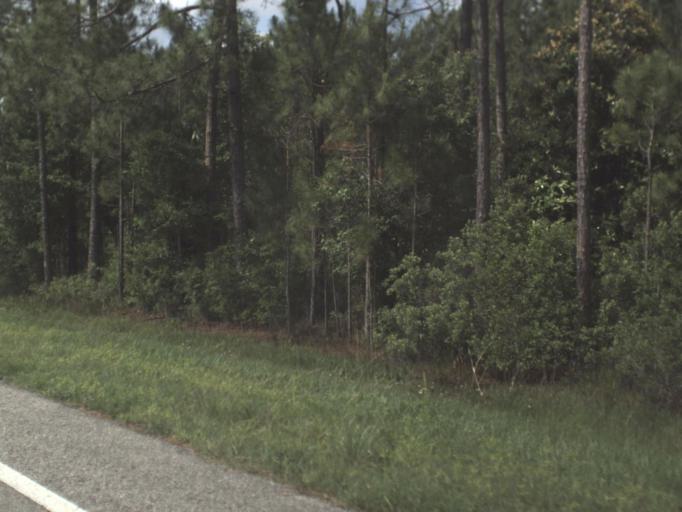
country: US
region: Florida
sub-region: Saint Johns County
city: Butler Beach
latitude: 29.7026
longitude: -81.2987
